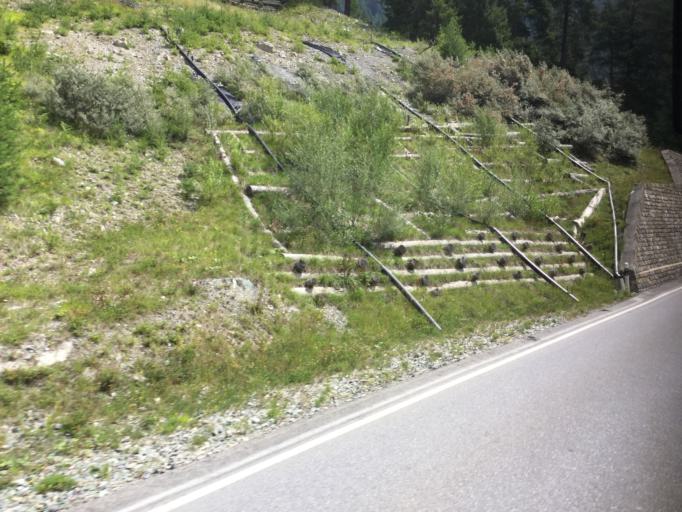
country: CH
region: Grisons
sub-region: Albula District
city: Tiefencastel
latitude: 46.6465
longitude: 9.5826
